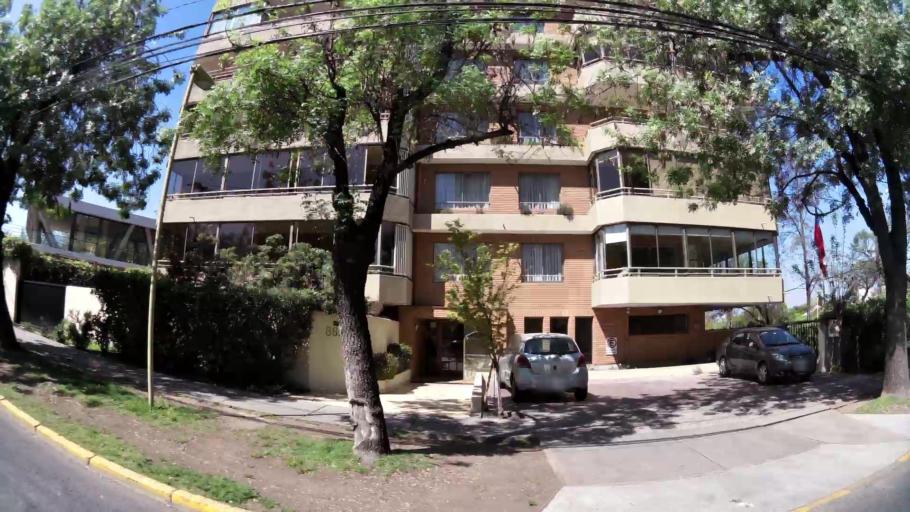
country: CL
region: Santiago Metropolitan
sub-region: Provincia de Santiago
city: Villa Presidente Frei, Nunoa, Santiago, Chile
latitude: -33.4097
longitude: -70.5442
